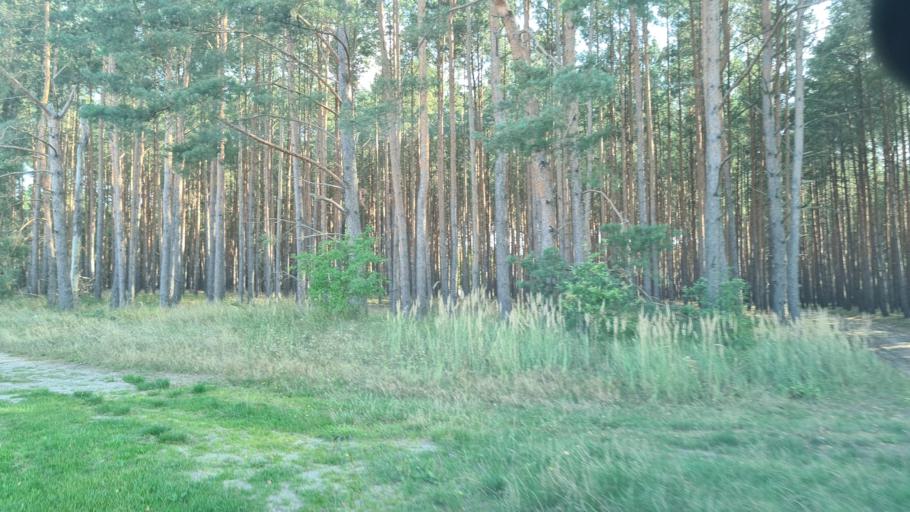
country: DE
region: Brandenburg
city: Luckenwalde
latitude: 52.1131
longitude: 13.2140
